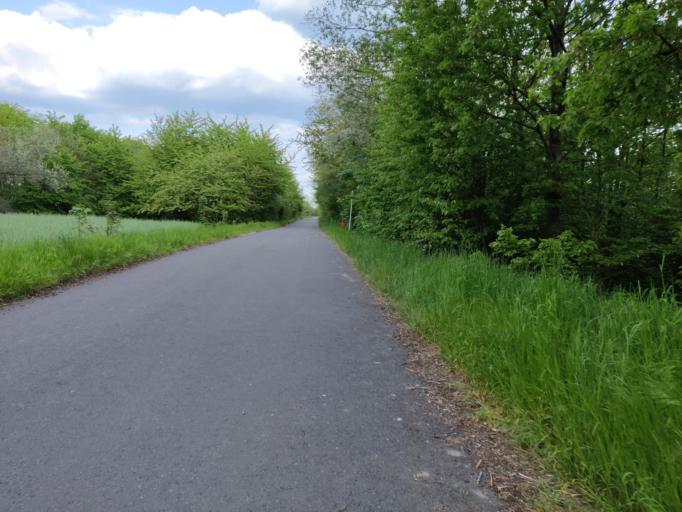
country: DE
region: Saxony
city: Grossposna
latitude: 51.2541
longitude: 12.4399
